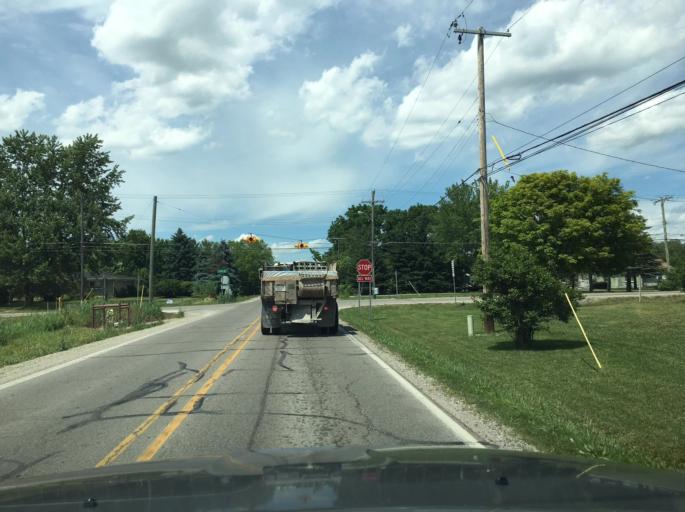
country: US
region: Michigan
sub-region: Macomb County
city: Romeo
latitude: 42.7598
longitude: -82.9610
